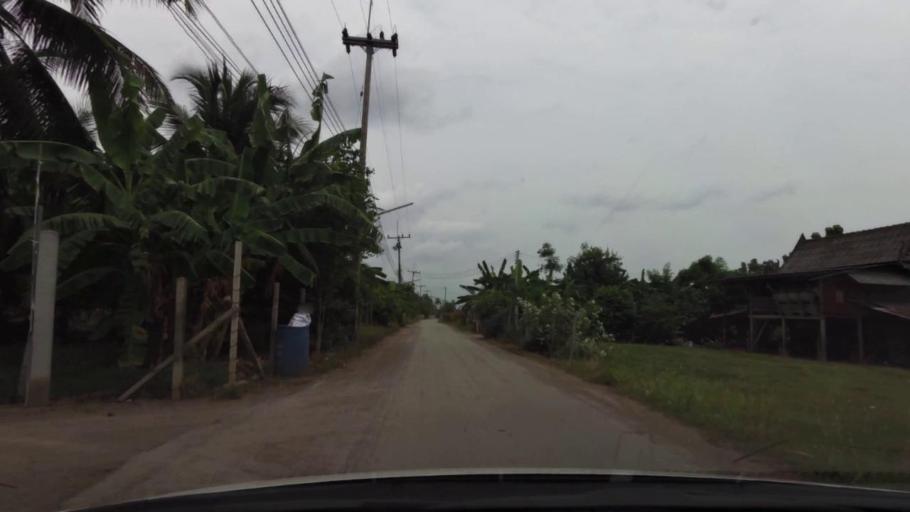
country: TH
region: Samut Sakhon
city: Ban Phaeo
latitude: 13.6241
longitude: 100.0269
